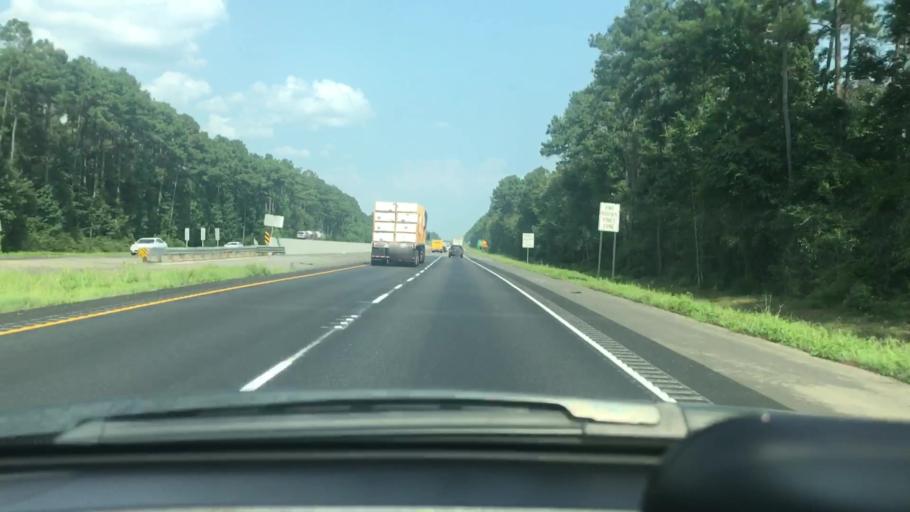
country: US
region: Louisiana
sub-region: Livingston Parish
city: Albany
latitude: 30.4745
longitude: -90.6589
